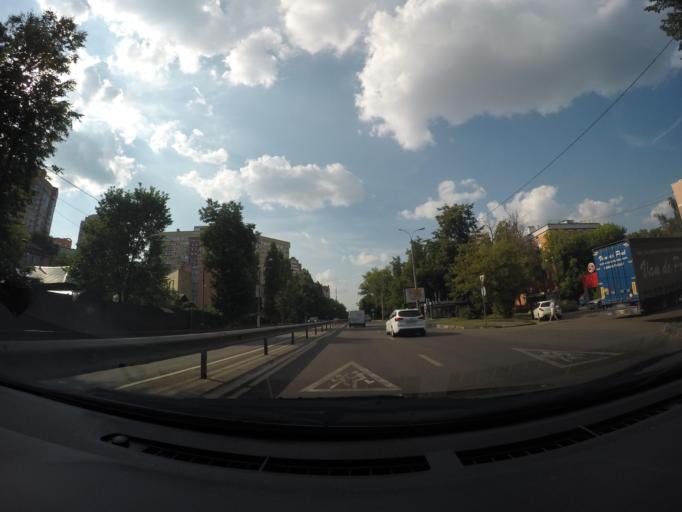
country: RU
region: Moscow
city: Zhulebino
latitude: 55.6898
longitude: 37.8703
